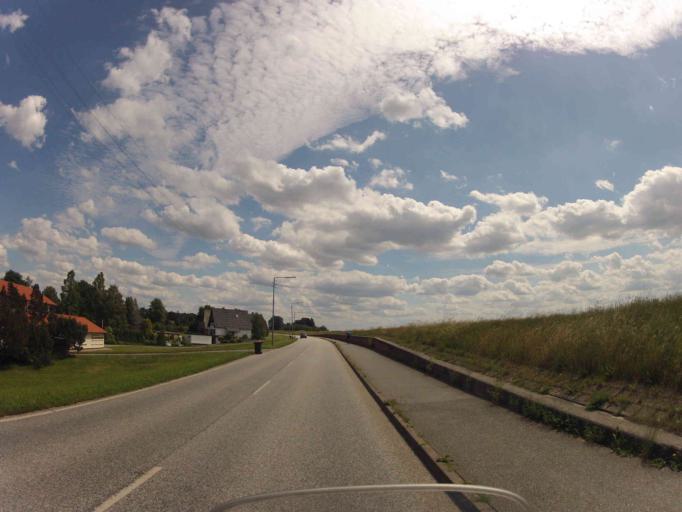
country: DE
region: Lower Saxony
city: Stelle
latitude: 53.4141
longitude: 10.1499
